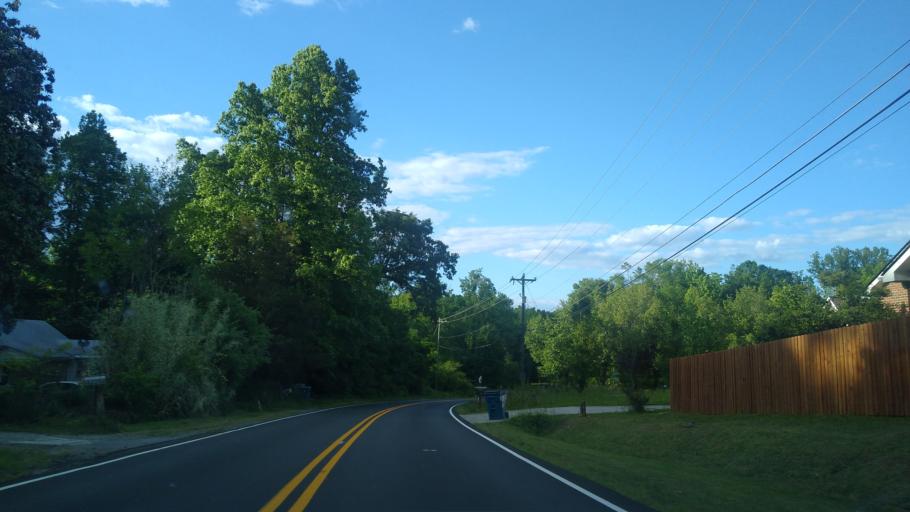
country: US
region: North Carolina
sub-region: Guilford County
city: McLeansville
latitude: 36.1533
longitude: -79.7391
